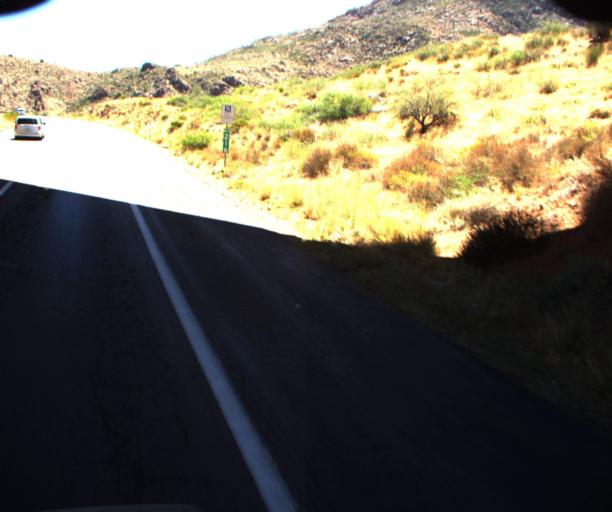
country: US
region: Arizona
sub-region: Gila County
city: Tonto Basin
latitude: 33.8373
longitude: -111.4711
